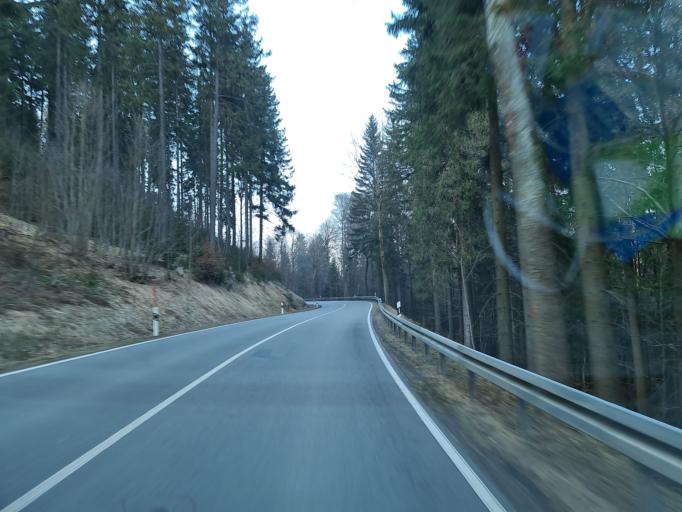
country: DE
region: Saxony
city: Sosa
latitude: 50.4645
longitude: 12.6301
